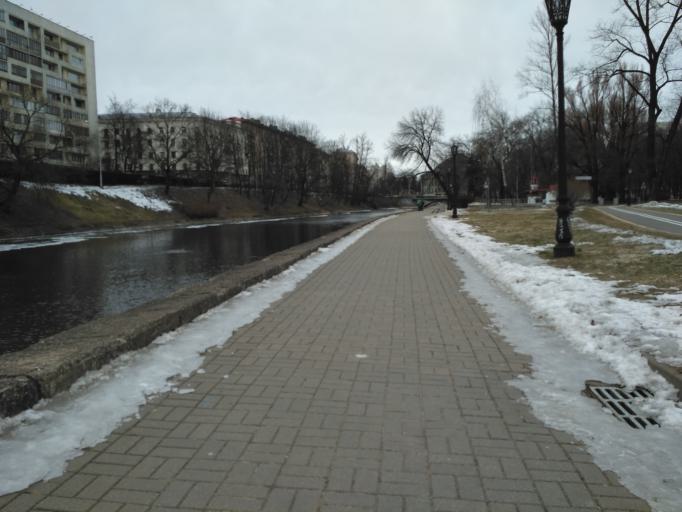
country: BY
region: Minsk
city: Minsk
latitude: 53.9005
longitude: 27.5716
